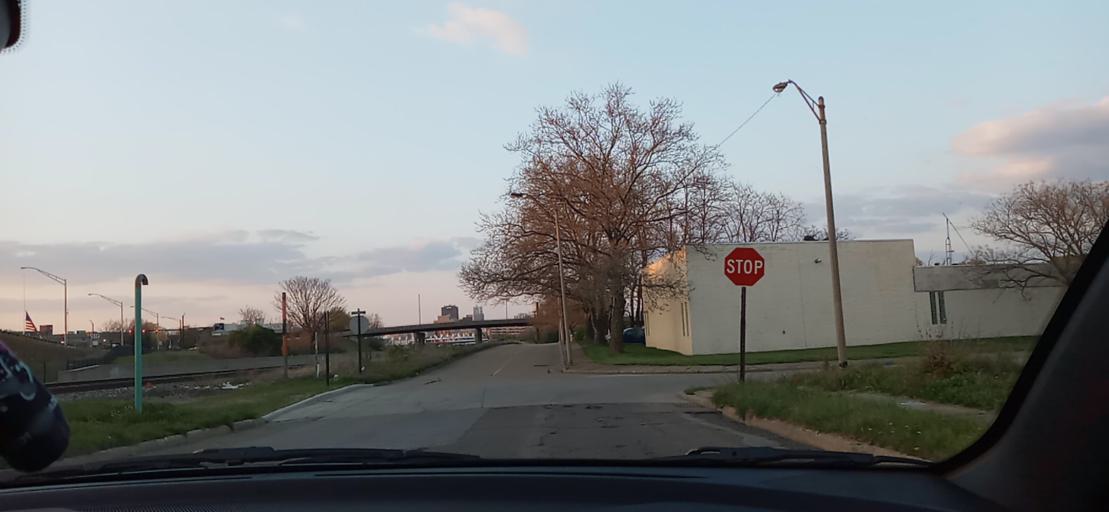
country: US
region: Ohio
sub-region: Summit County
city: Akron
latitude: 41.0634
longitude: -81.5241
